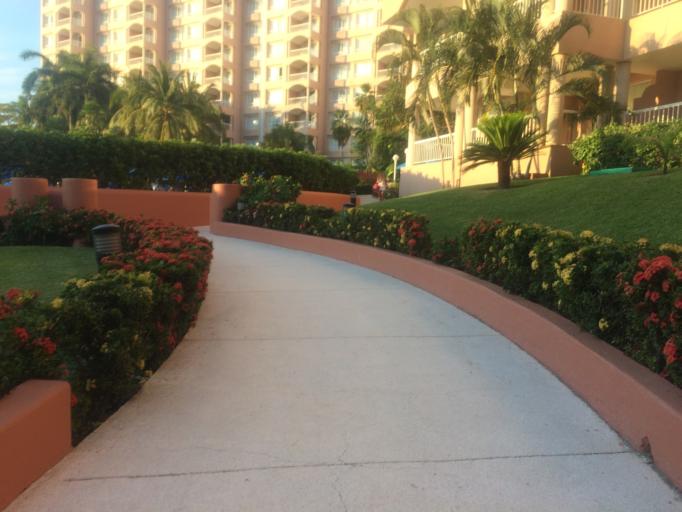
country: MX
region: Guerrero
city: Ixtapa
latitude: 17.6780
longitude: -101.6422
